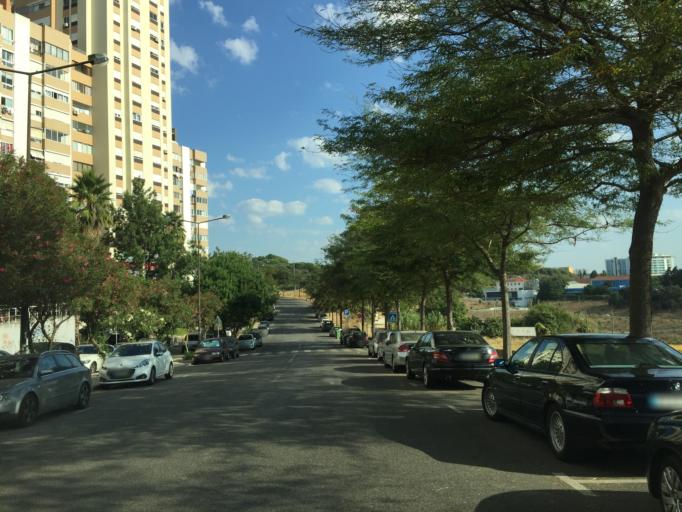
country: PT
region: Lisbon
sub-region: Lisbon
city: Lisbon
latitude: 38.7426
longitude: -9.1275
